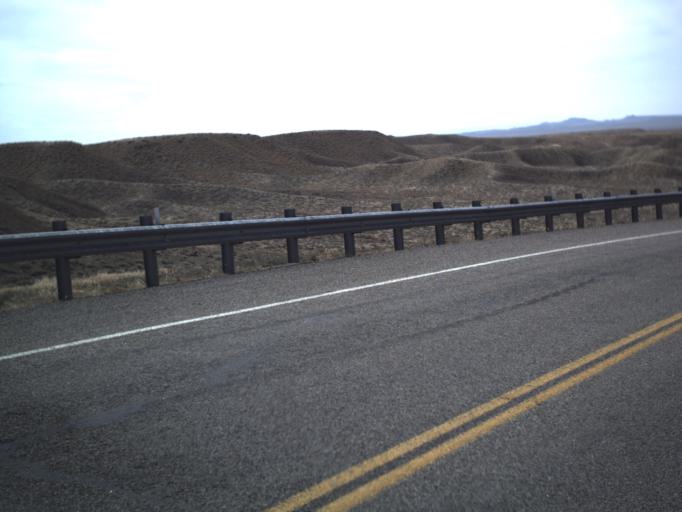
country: US
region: Utah
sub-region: Grand County
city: Moab
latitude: 38.9367
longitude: -109.8293
